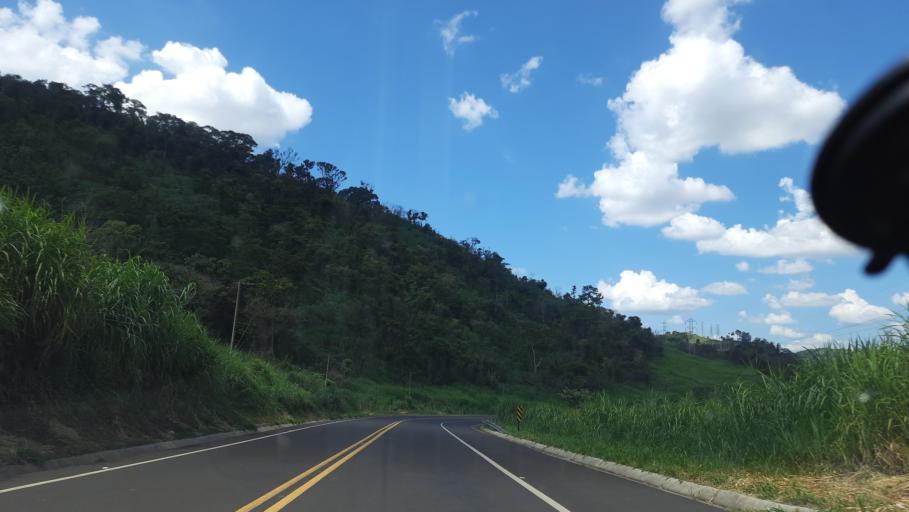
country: BR
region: Sao Paulo
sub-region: Sao Jose Do Rio Pardo
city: Sao Jose do Rio Pardo
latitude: -21.6042
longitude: -46.9600
